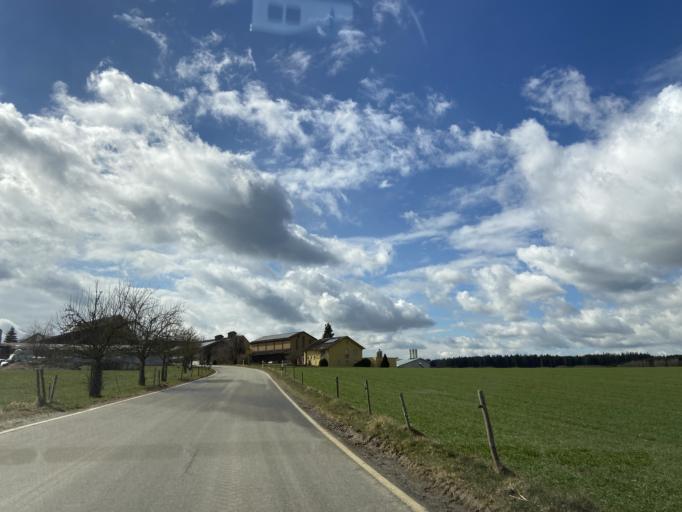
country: DE
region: Baden-Wuerttemberg
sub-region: Tuebingen Region
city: Pfullendorf
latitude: 47.9665
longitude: 9.3121
